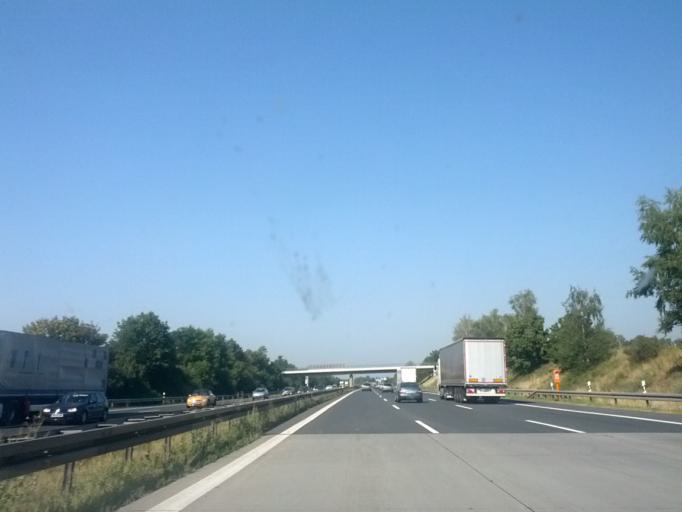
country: DE
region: Brandenburg
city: Mittenwalde
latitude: 52.3185
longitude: 13.5289
